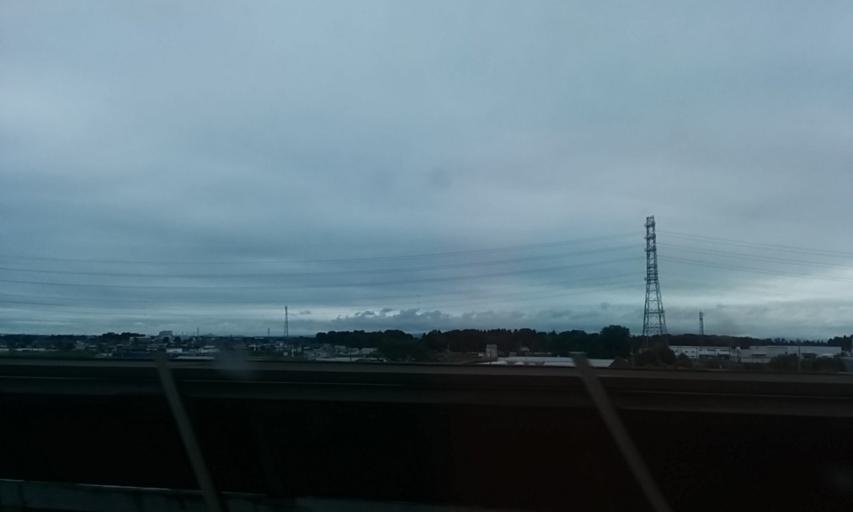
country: JP
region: Tochigi
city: Kaminokawa
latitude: 36.4220
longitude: 139.8641
